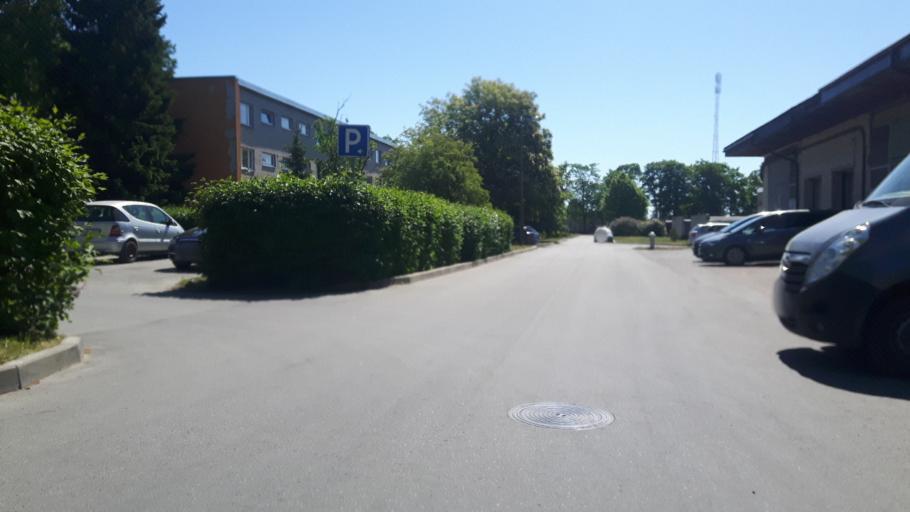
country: EE
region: Harju
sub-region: Saku vald
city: Saku
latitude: 59.2979
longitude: 24.6635
